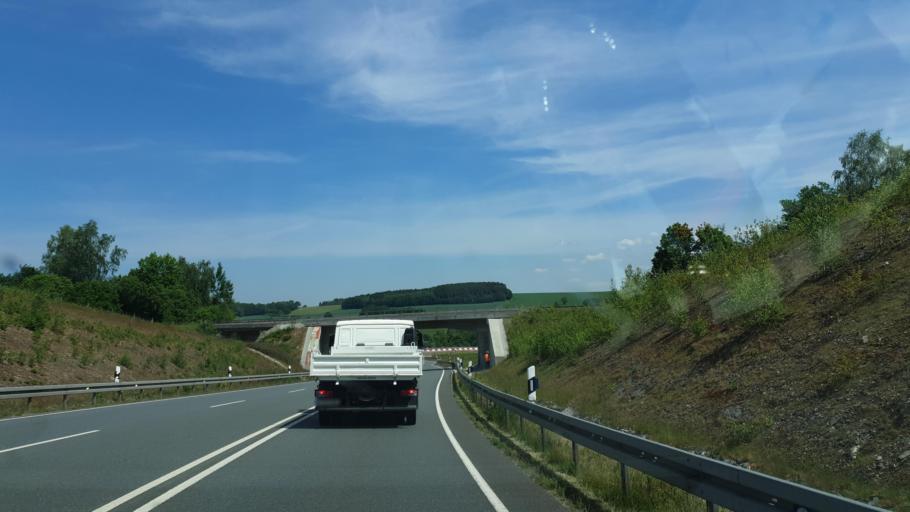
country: DE
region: Saxony
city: Rodewisch
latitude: 50.5337
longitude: 12.3925
